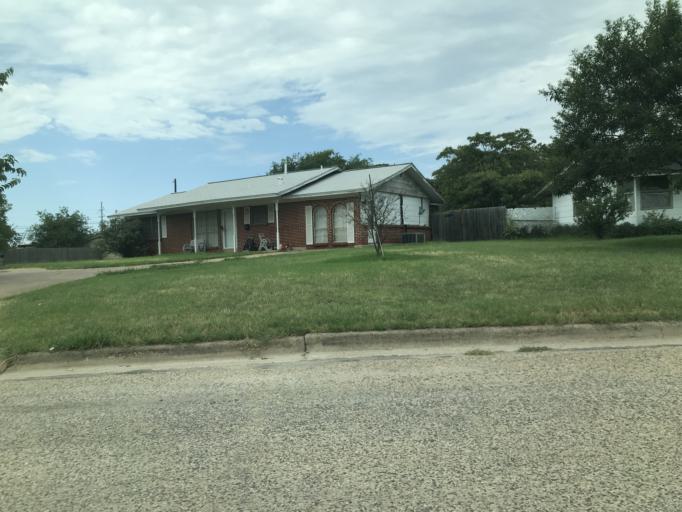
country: US
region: Texas
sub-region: Taylor County
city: Abilene
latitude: 32.4493
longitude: -99.6964
